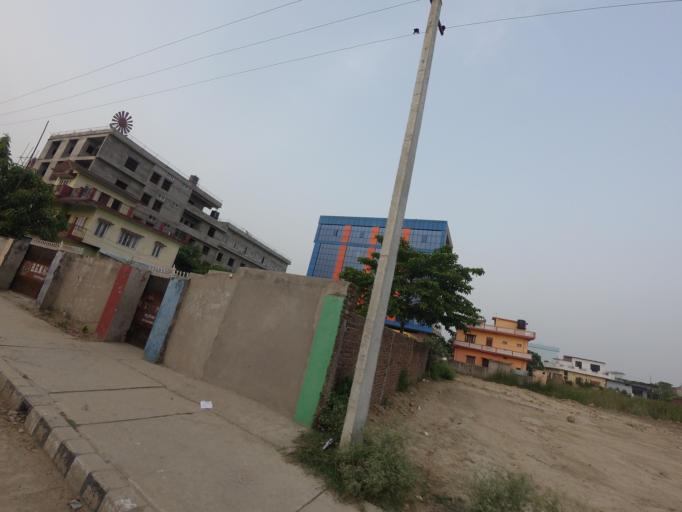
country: NP
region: Western Region
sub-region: Lumbini Zone
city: Bhairahawa
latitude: 27.5092
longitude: 83.4609
